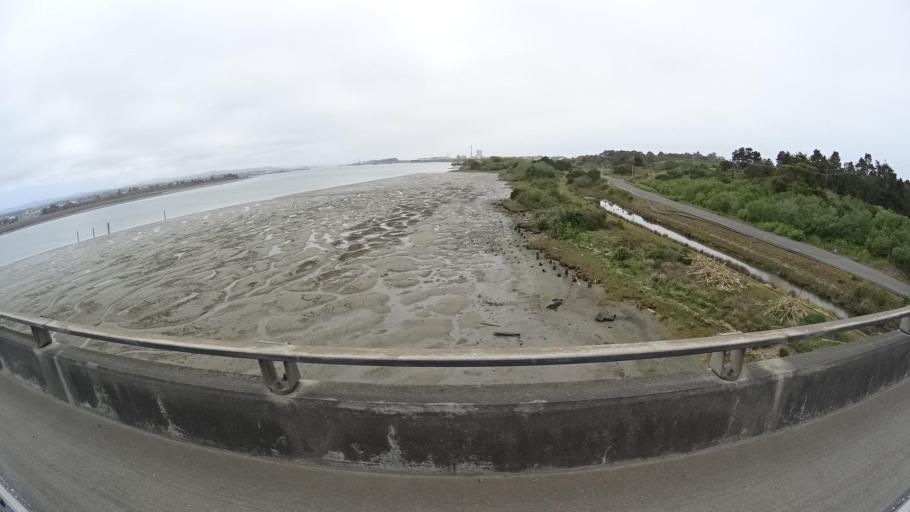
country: US
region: California
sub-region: Humboldt County
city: Eureka
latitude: 40.8240
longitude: -124.1737
